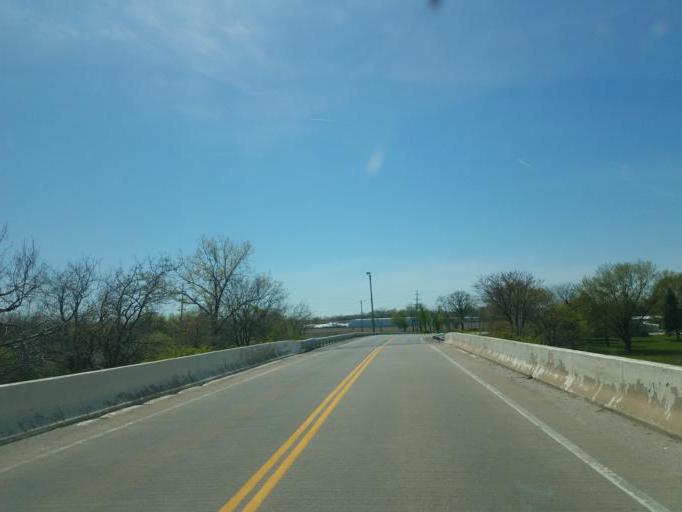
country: US
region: Ohio
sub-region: Ottawa County
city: Port Clinton
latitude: 41.5092
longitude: -82.8828
